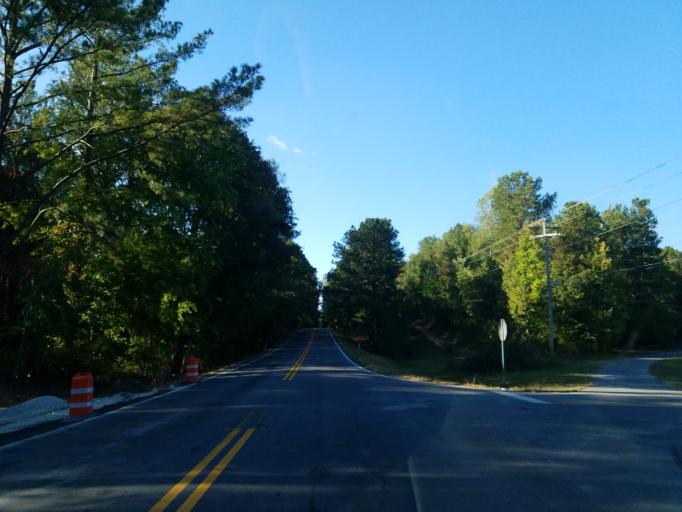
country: US
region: Georgia
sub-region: Bartow County
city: Emerson
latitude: 34.0732
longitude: -84.8293
